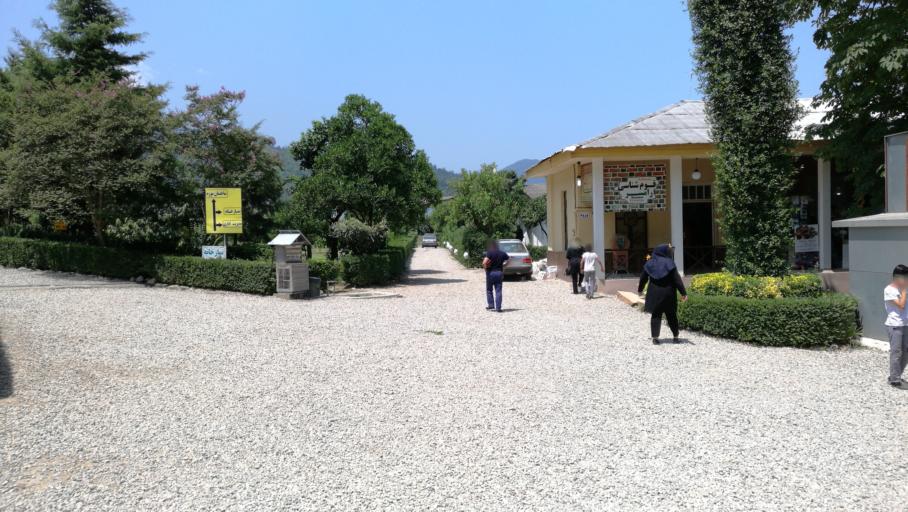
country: IR
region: Mazandaran
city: Ramsar
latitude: 36.9043
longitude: 50.6547
